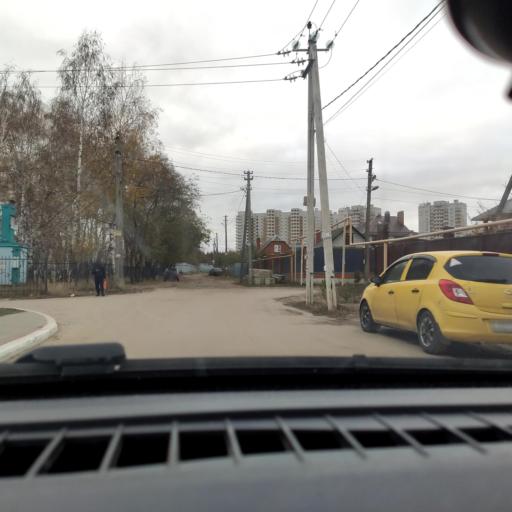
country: RU
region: Voronezj
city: Podgornoye
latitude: 51.7295
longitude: 39.1620
